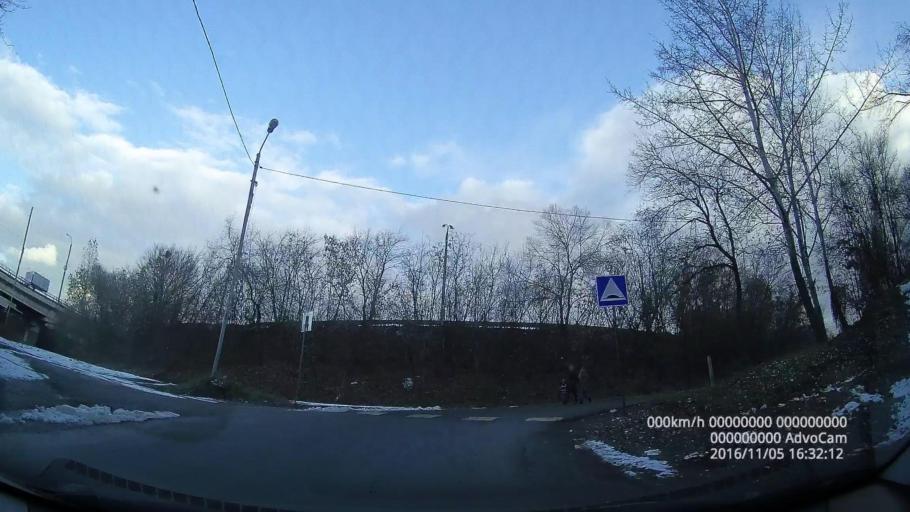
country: RU
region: Voronezj
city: Voronezh
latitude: 51.6868
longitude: 39.2180
